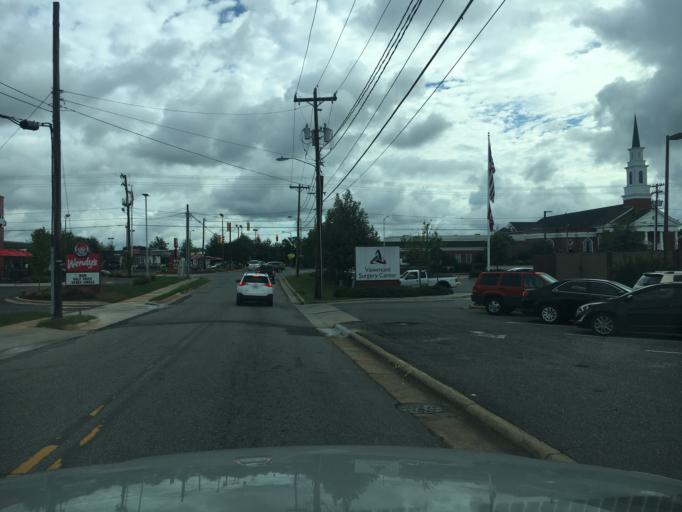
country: US
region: North Carolina
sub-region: Catawba County
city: Hickory
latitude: 35.7498
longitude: -81.3364
